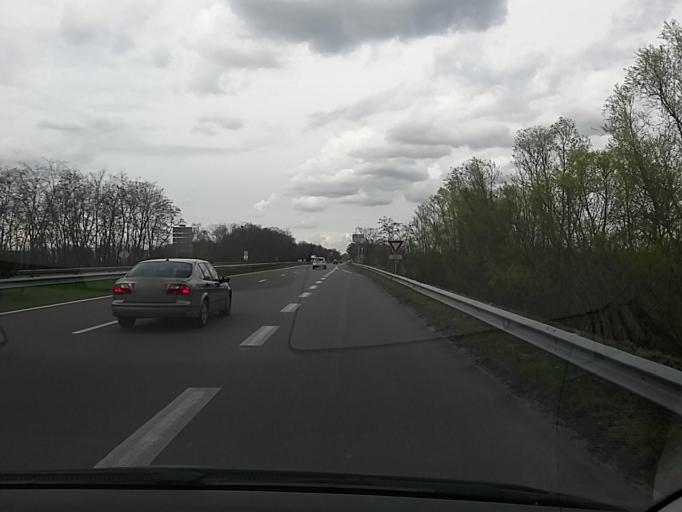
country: FR
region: Picardie
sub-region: Departement de l'Oise
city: Le Meux
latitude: 49.3552
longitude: 2.7566
